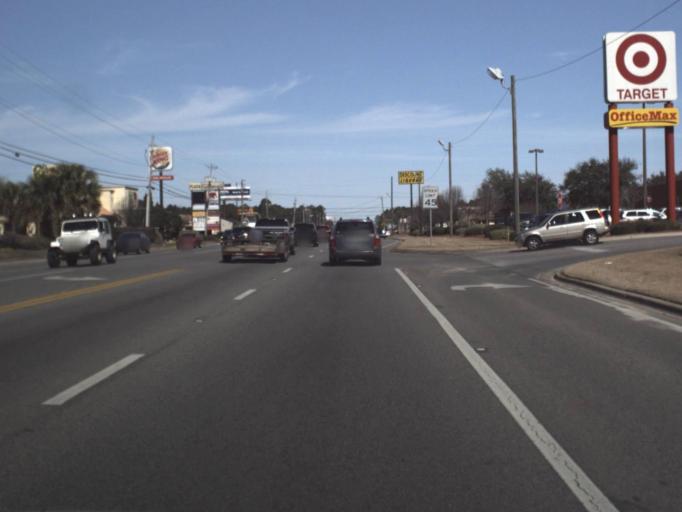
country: US
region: Florida
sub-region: Bay County
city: Hiland Park
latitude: 30.1906
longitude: -85.6499
